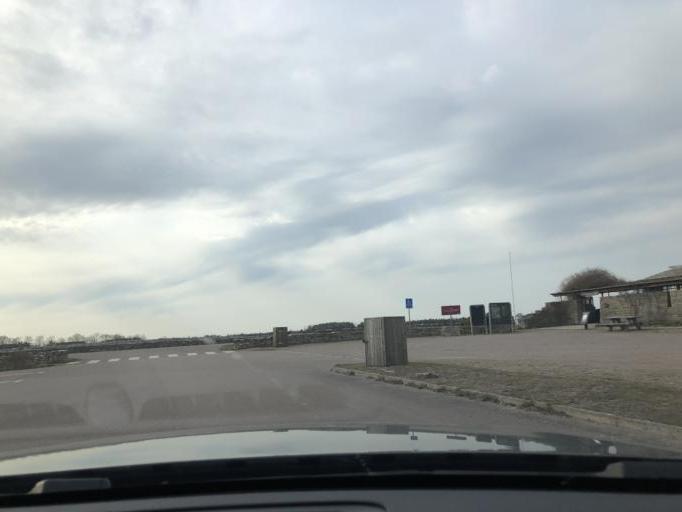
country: SE
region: Kalmar
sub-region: Morbylanga Kommun
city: Moerbylanga
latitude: 56.2925
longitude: 16.4842
